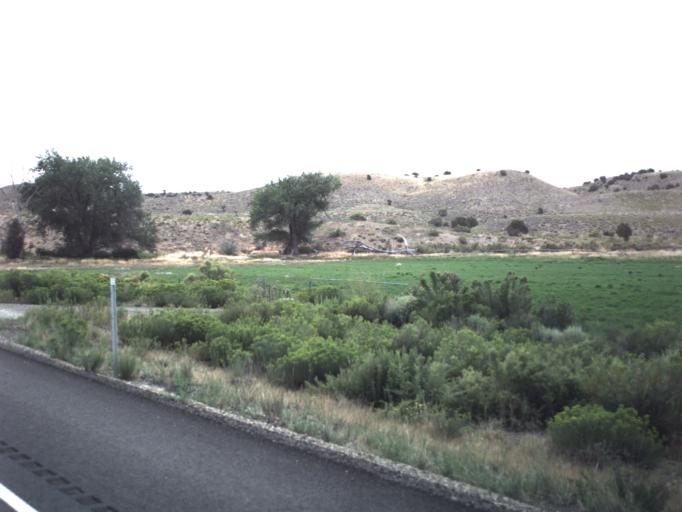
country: US
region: Utah
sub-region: Carbon County
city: Wellington
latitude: 39.5497
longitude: -110.6651
